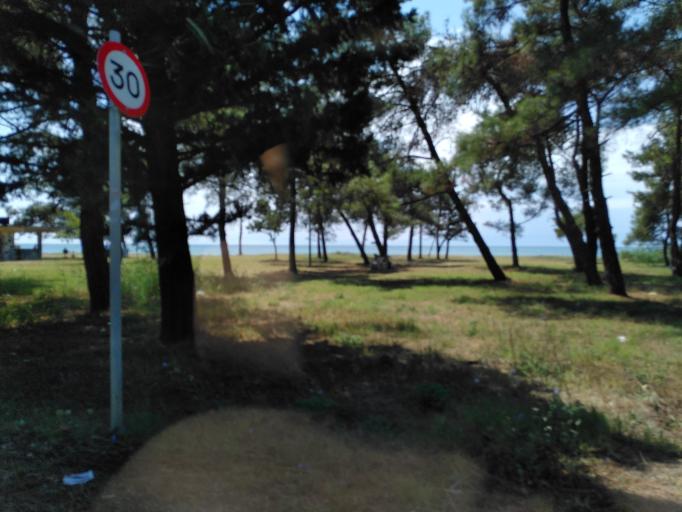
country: GR
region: Central Macedonia
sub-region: Nomos Thessalonikis
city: Nea Michaniona
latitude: 40.4296
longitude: 22.8772
